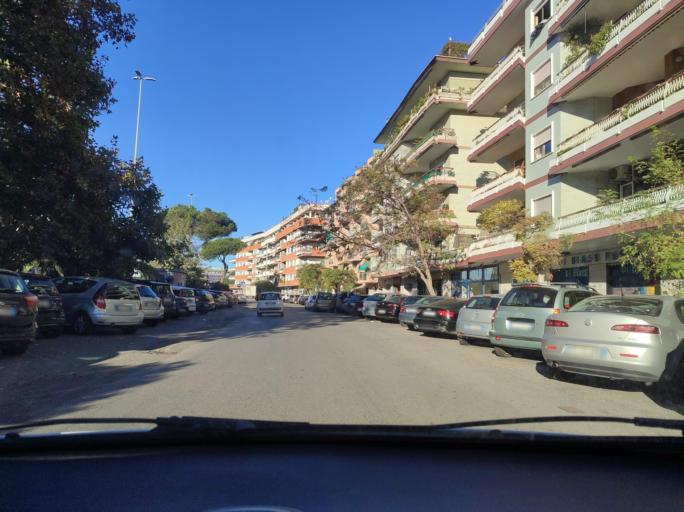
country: IT
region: Latium
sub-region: Citta metropolitana di Roma Capitale
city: Lido di Ostia
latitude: 41.7384
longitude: 12.2794
